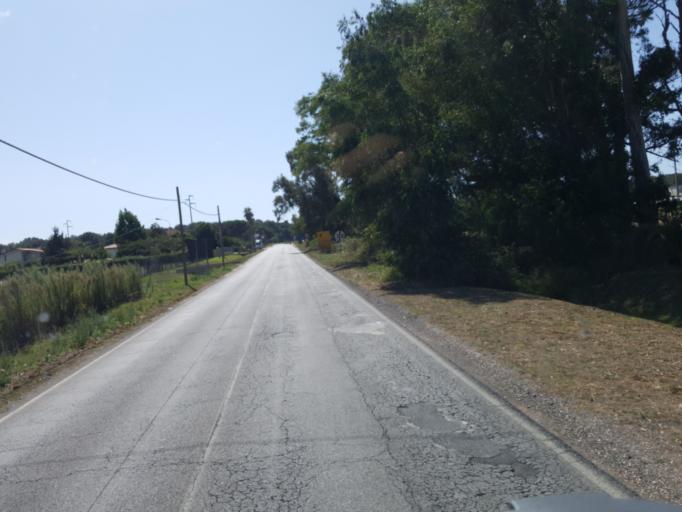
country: IT
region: Latium
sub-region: Provincia di Latina
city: Sabaudia
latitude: 41.3410
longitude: 13.0847
